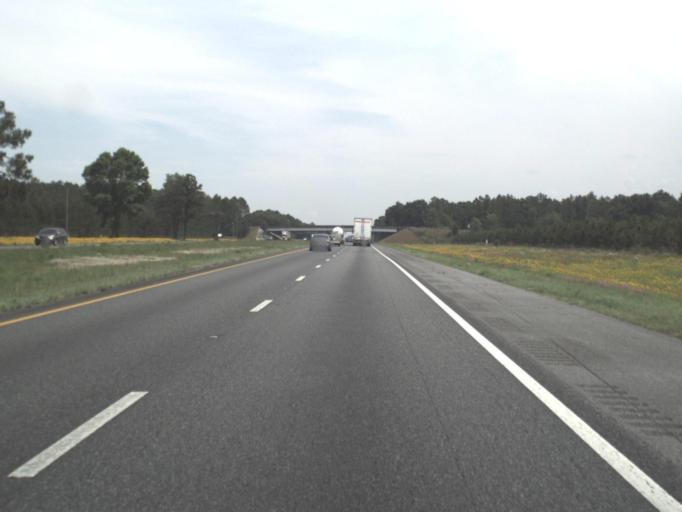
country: US
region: Florida
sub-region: Suwannee County
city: Live Oak
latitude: 30.3140
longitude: -82.9381
